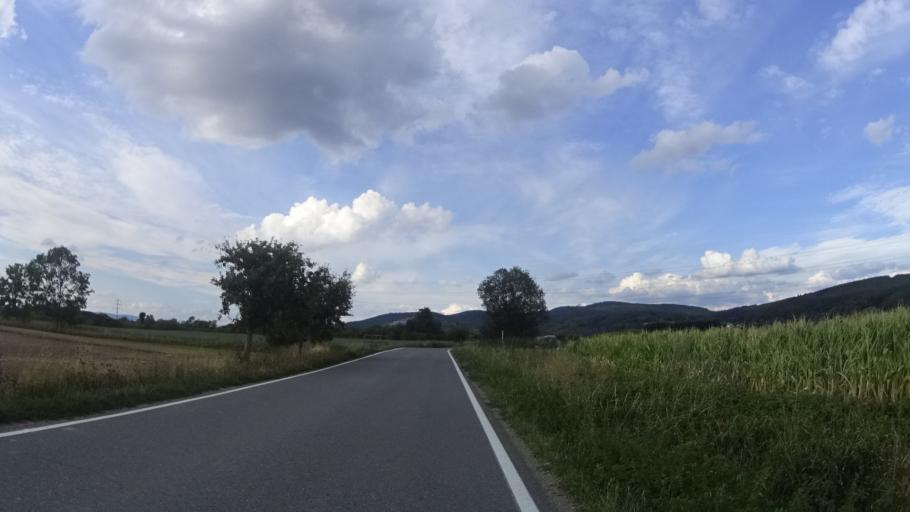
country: CZ
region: Olomoucky
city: Dubicko
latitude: 49.8382
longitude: 16.9375
